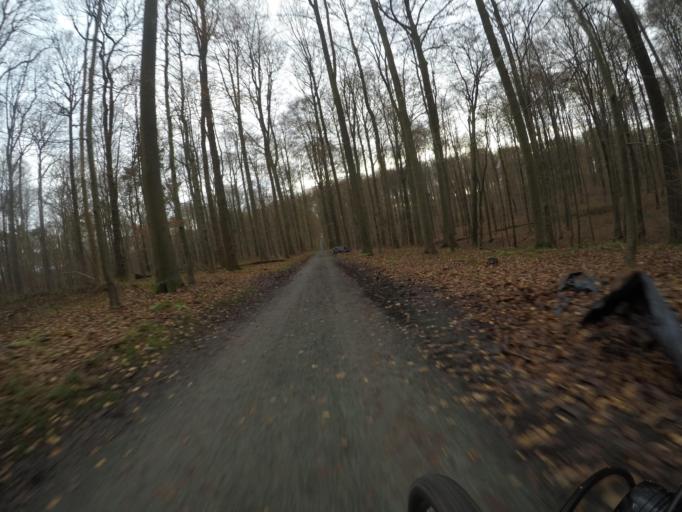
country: BE
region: Flanders
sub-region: Provincie Vlaams-Brabant
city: Hoeilaart
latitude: 50.7522
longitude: 4.4421
